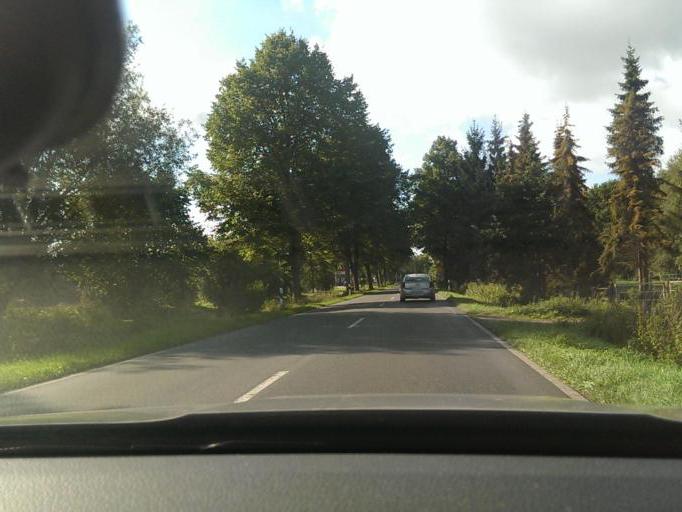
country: DE
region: Lower Saxony
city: Isernhagen Farster Bauerschaft
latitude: 52.4758
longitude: 9.8563
